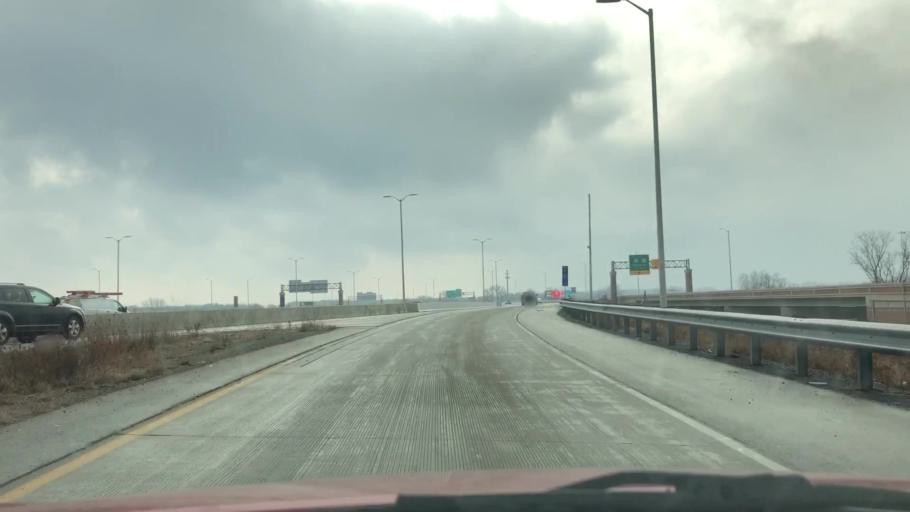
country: US
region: Wisconsin
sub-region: Brown County
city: Howard
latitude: 44.5365
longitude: -88.0798
